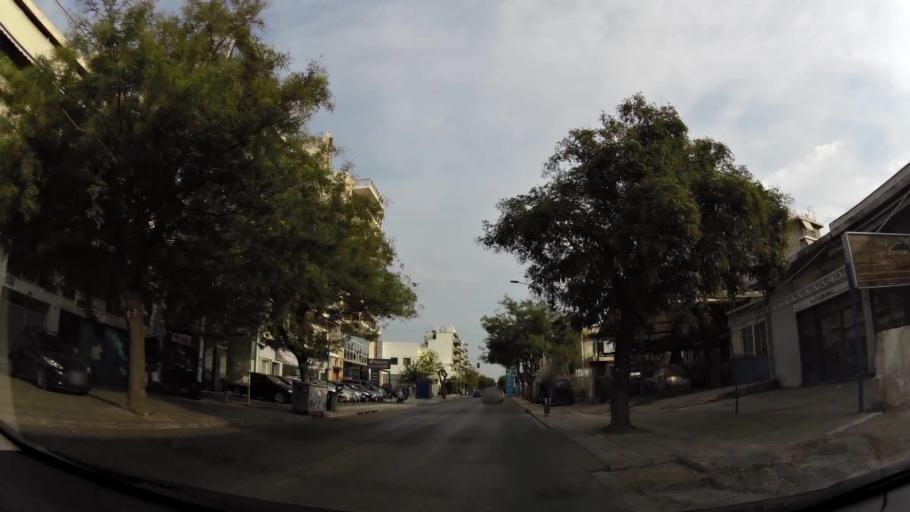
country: GR
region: Attica
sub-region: Nomarchia Athinas
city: Agioi Anargyroi
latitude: 38.0142
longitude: 23.7202
